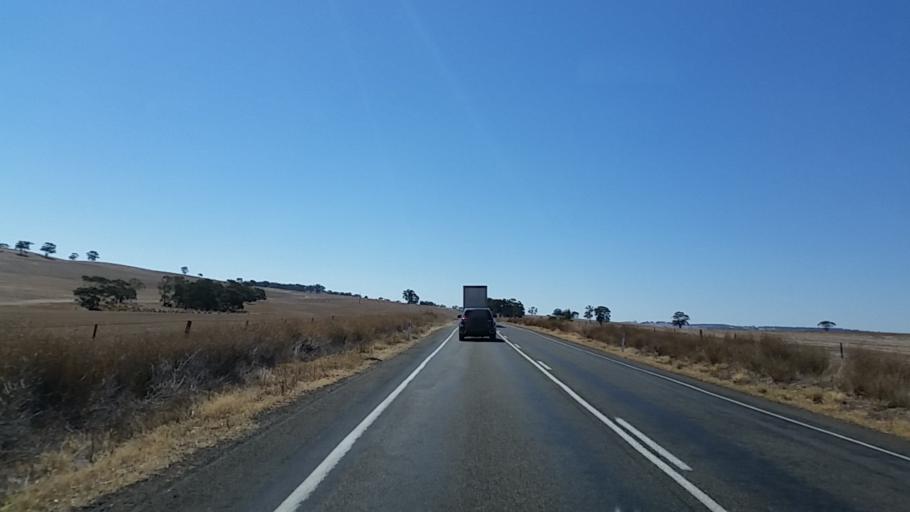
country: AU
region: South Australia
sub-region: Clare and Gilbert Valleys
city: Clare
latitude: -34.0446
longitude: 138.7991
